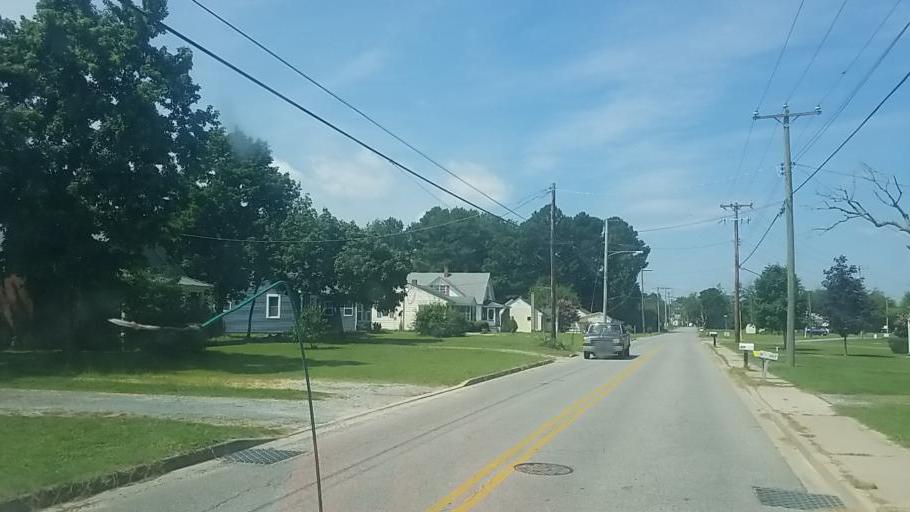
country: US
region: Maryland
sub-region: Caroline County
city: Denton
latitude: 38.8836
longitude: -75.8168
